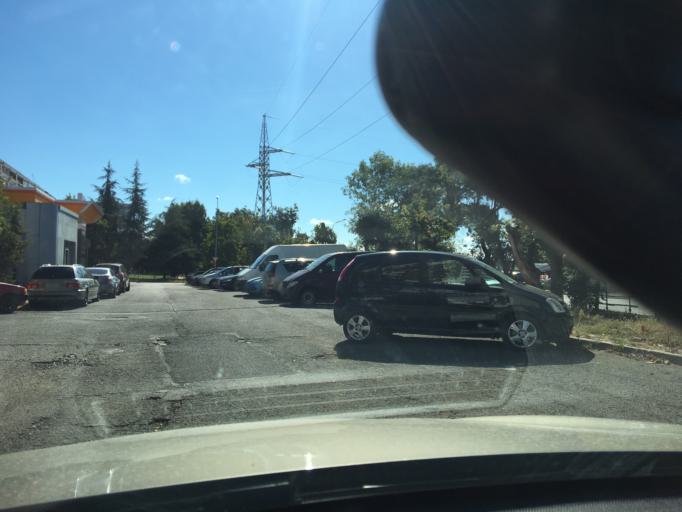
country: BG
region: Burgas
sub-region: Obshtina Burgas
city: Burgas
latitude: 42.5165
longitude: 27.4494
